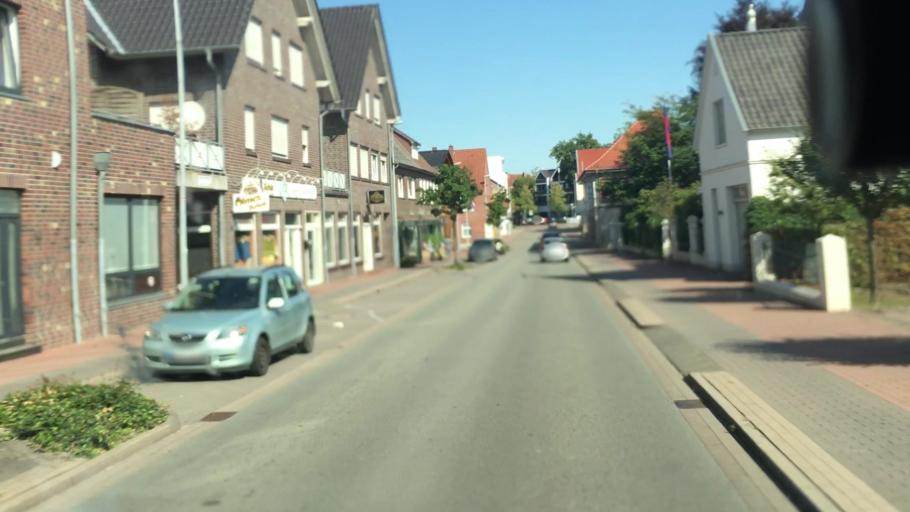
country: DE
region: Lower Saxony
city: Lohne
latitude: 52.6609
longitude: 8.2401
